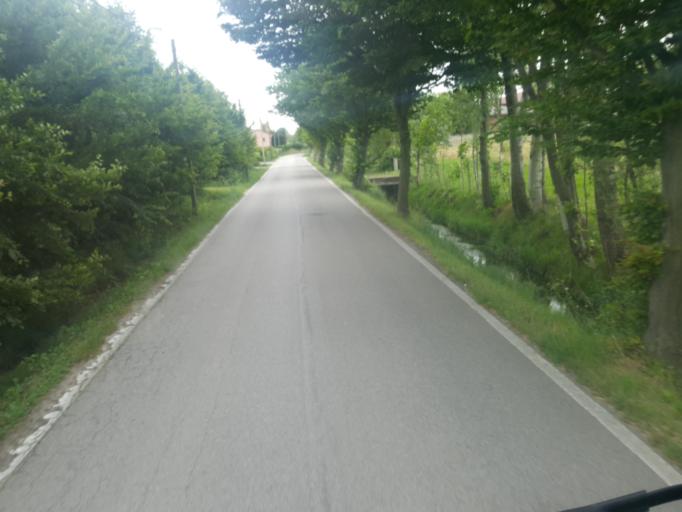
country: IT
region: Veneto
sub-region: Provincia di Treviso
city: Resana
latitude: 45.6316
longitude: 11.9492
